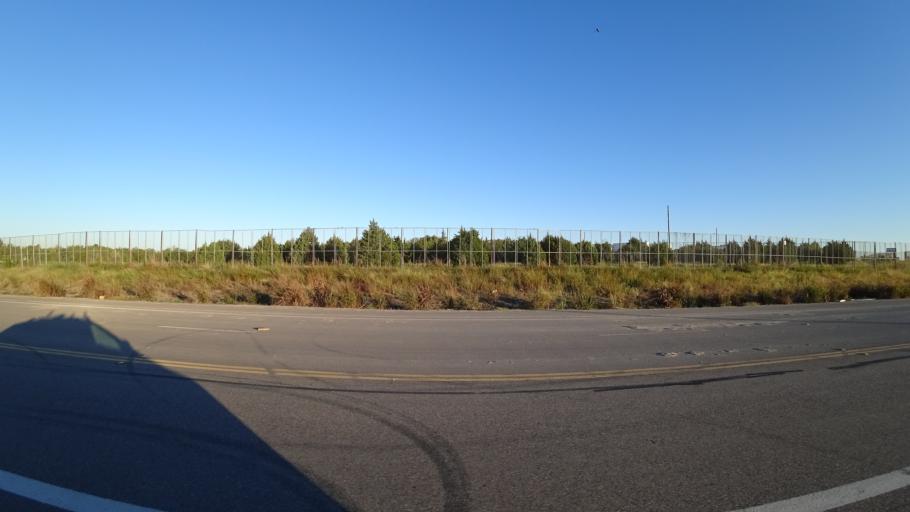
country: US
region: Texas
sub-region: Travis County
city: Manor
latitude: 30.3307
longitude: -97.6037
